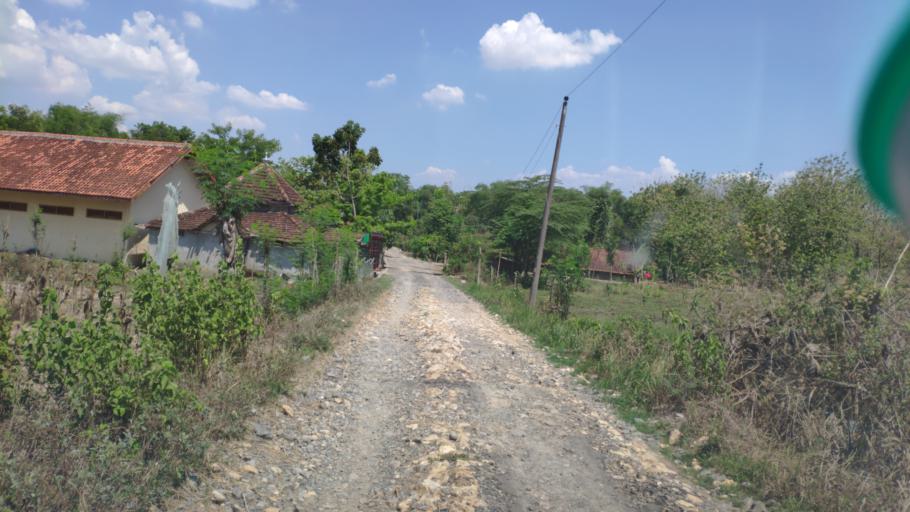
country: ID
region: Central Java
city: Galuk
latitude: -7.1084
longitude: 111.4996
